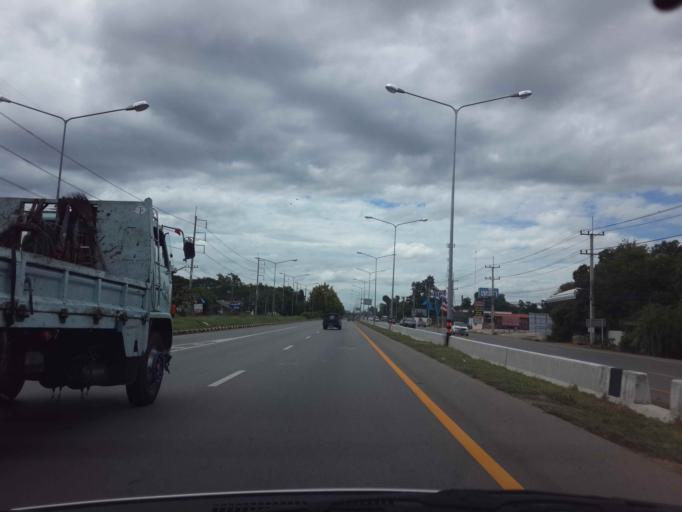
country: TH
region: Phetchaburi
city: Khao Yoi
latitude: 13.1484
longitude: 99.8538
